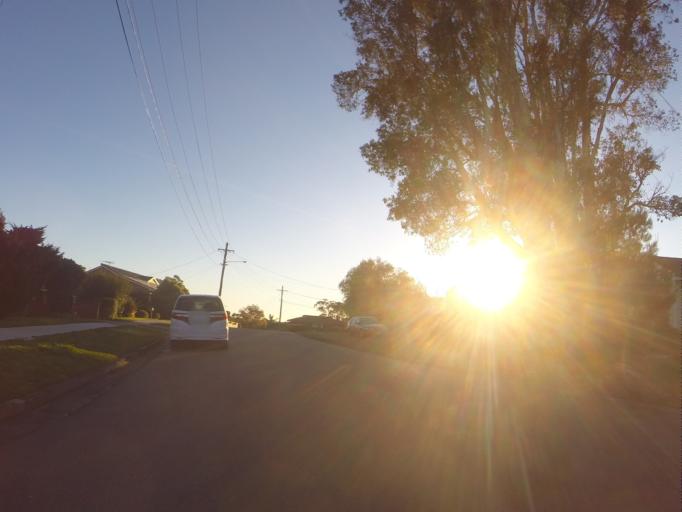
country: AU
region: New South Wales
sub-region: Sutherland Shire
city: Engadine
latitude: -34.0475
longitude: 151.0129
